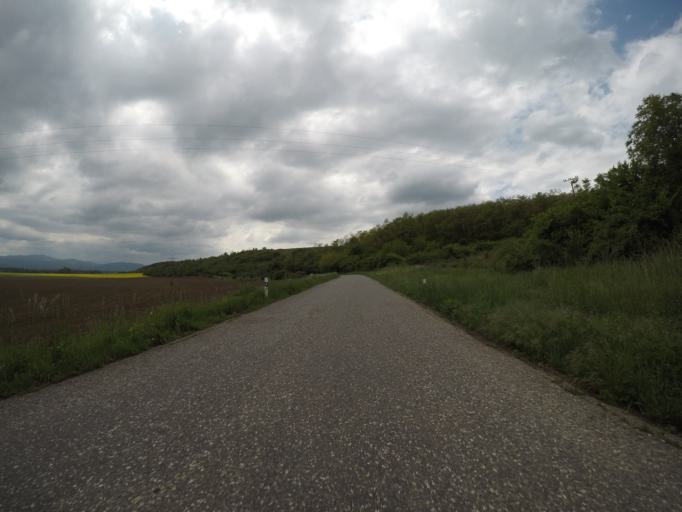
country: SK
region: Banskobystricky
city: Dudince
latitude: 48.1091
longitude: 18.8704
